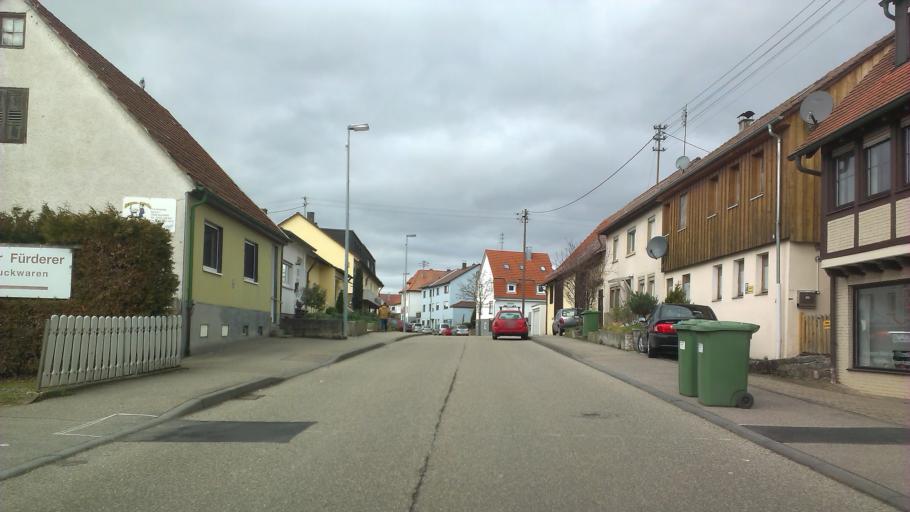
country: DE
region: Baden-Wuerttemberg
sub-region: Karlsruhe Region
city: Illingen
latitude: 48.9577
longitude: 8.9190
